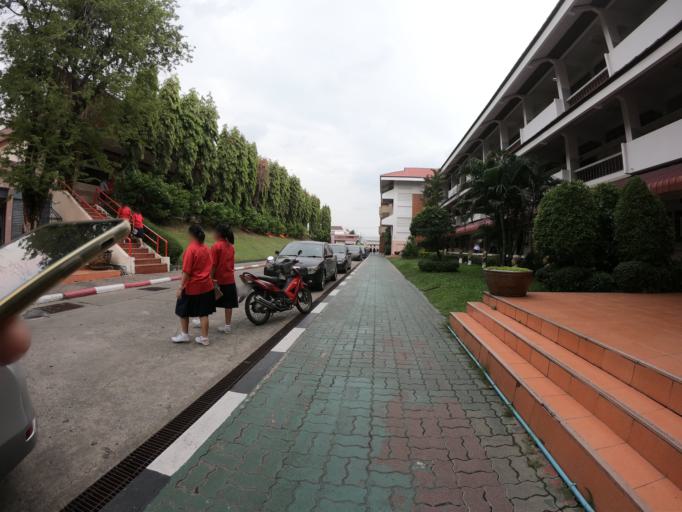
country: TH
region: Bangkok
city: Lat Phrao
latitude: 13.8254
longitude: 100.6165
